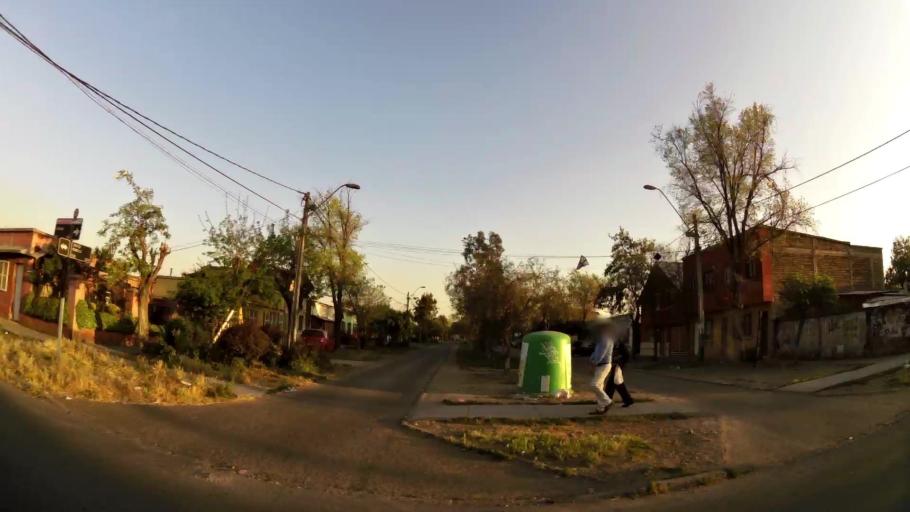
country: CL
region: Santiago Metropolitan
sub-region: Provincia de Santiago
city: Santiago
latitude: -33.5034
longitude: -70.6301
